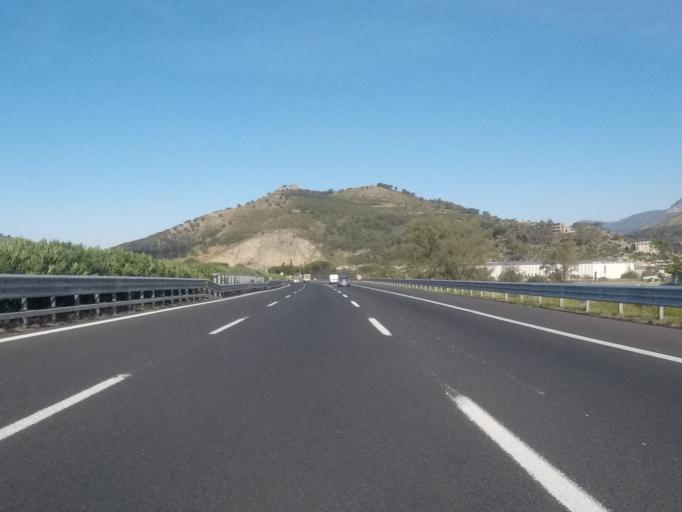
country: IT
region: Campania
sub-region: Provincia di Salerno
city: Casali-San Potito
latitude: 40.7693
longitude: 14.6726
